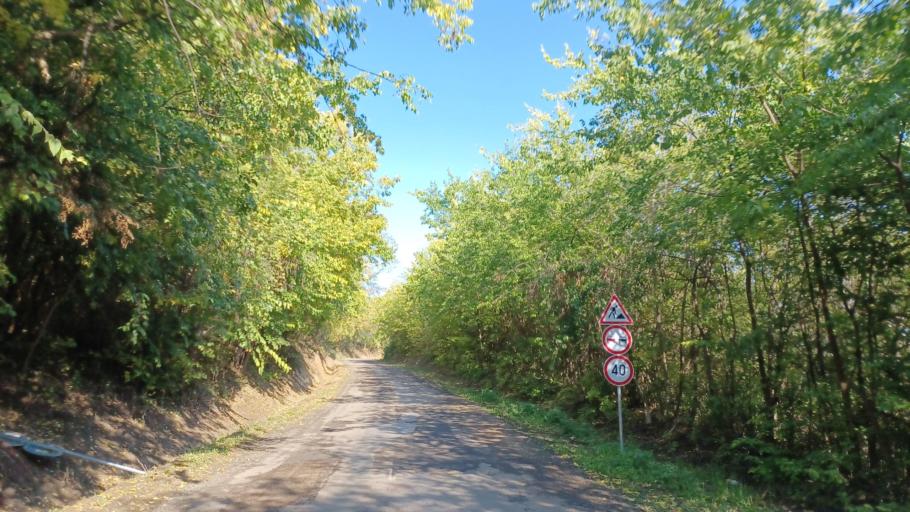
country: HU
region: Tolna
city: Szedres
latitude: 46.5368
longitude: 18.5924
